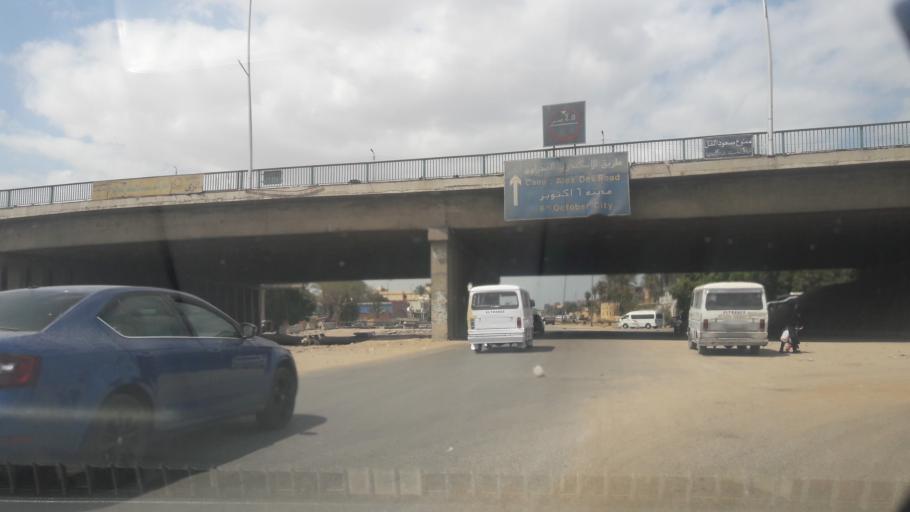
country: EG
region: Al Jizah
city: Al Jizah
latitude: 29.9546
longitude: 31.1548
